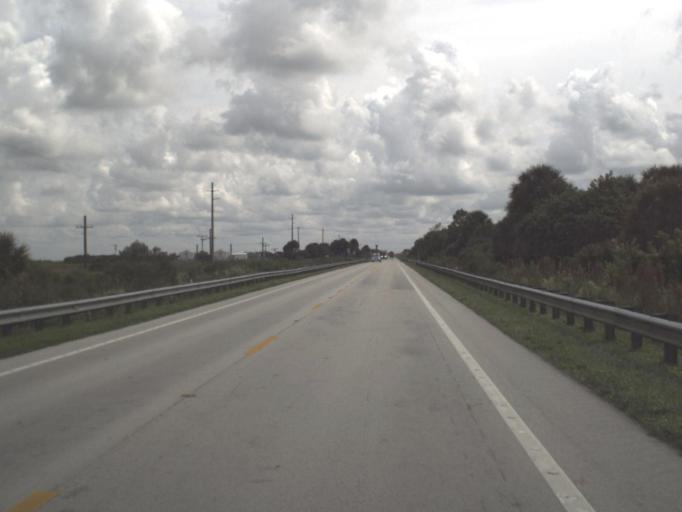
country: US
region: Florida
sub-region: Glades County
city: Buckhead Ridge
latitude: 27.2361
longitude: -81.0577
